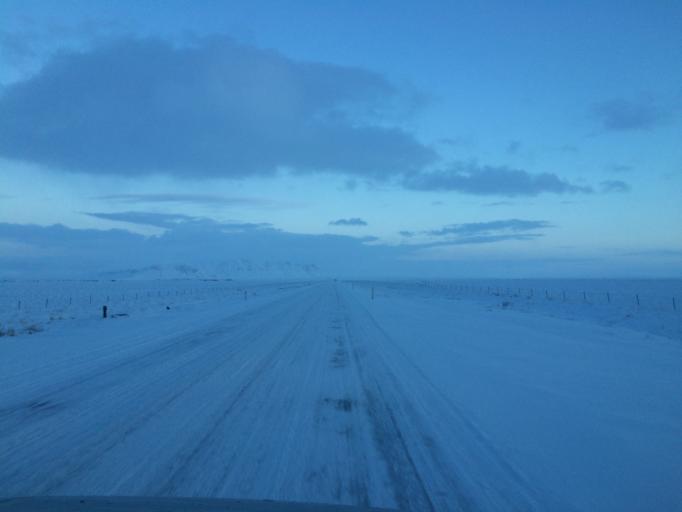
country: IS
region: South
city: Selfoss
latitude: 63.8683
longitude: -21.1011
